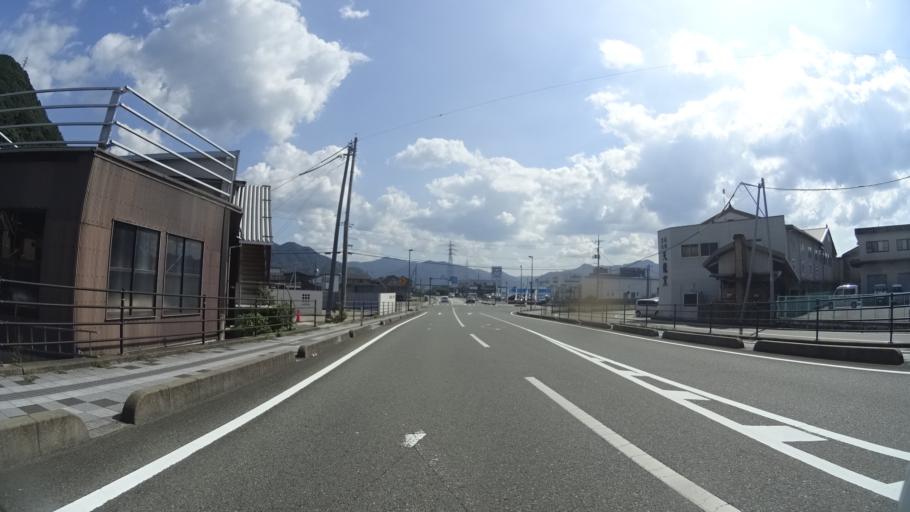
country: JP
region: Yamaguchi
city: Hagi
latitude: 34.4221
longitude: 131.4126
